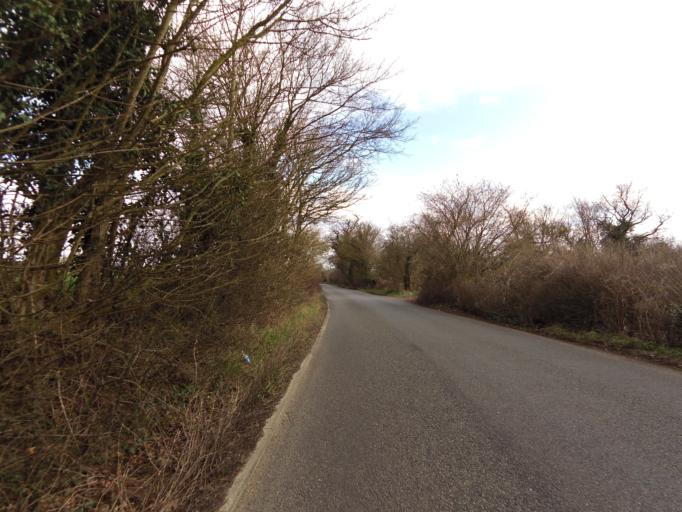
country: GB
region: England
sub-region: Suffolk
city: Ipswich
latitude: 52.0896
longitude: 1.1564
